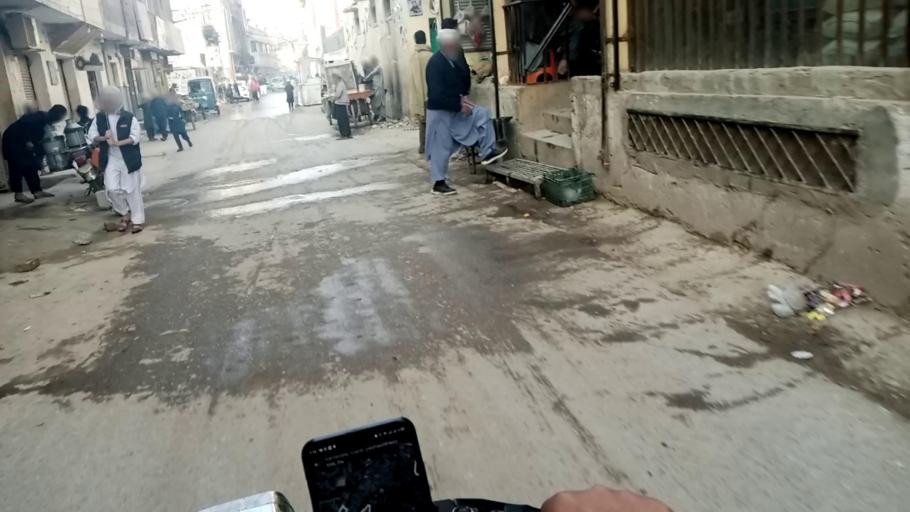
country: PK
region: Khyber Pakhtunkhwa
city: Peshawar
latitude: 34.0038
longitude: 71.4726
